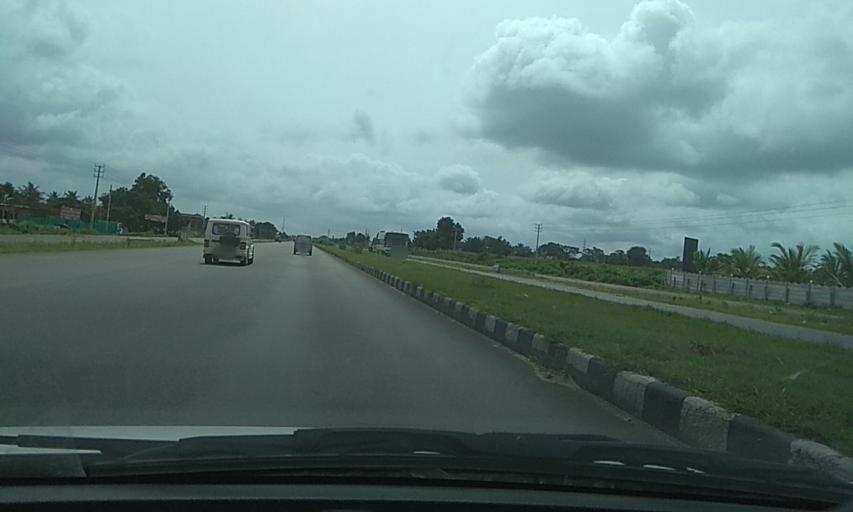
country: IN
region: Karnataka
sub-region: Davanagere
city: Mayakonda
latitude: 14.3979
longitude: 76.0263
